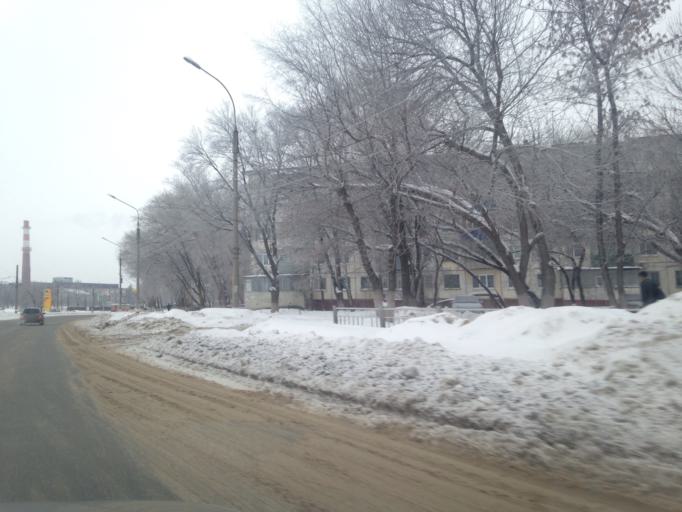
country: RU
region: Ulyanovsk
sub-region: Ulyanovskiy Rayon
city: Ulyanovsk
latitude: 54.2988
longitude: 48.3394
